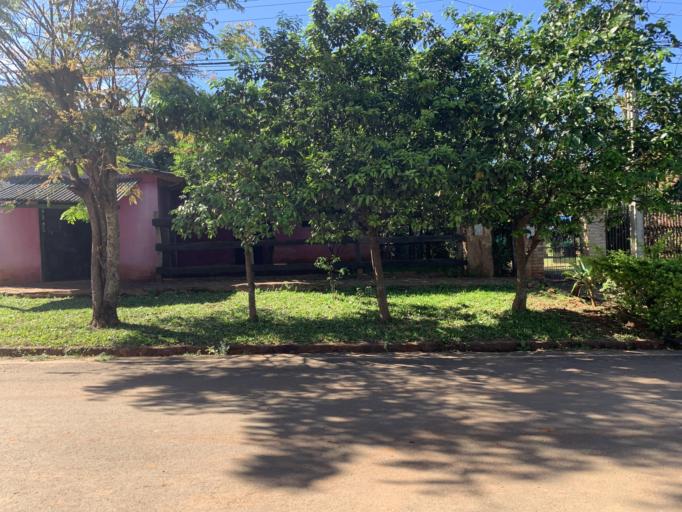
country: PY
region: Misiones
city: San Juan Bautista
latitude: -26.6775
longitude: -57.1454
